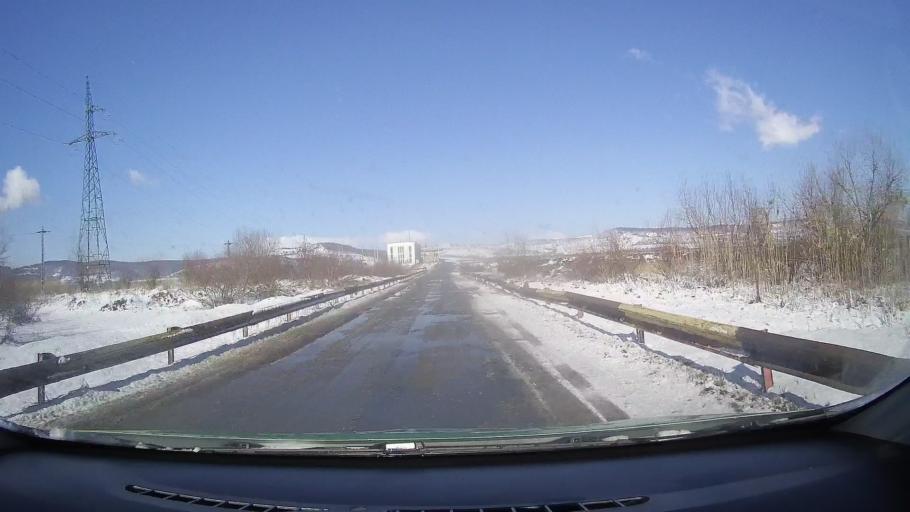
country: RO
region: Sibiu
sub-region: Comuna Avrig
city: Avrig
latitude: 45.7404
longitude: 24.3918
